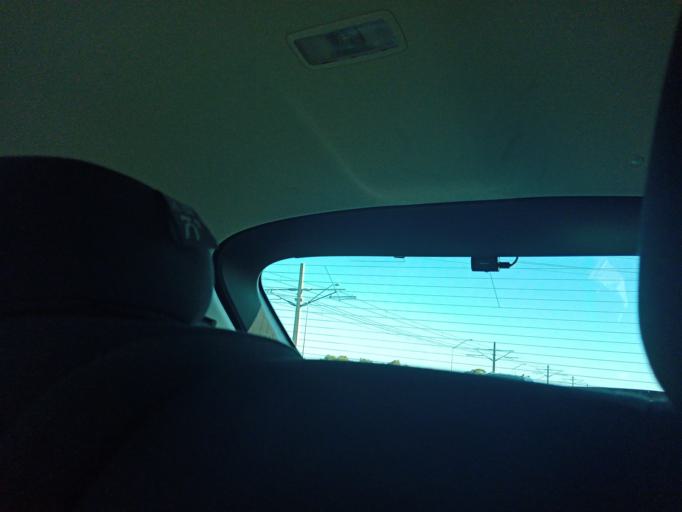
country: AU
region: Western Australia
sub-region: City of Cockburn
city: City of Cockburn
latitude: -32.0948
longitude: 115.8491
